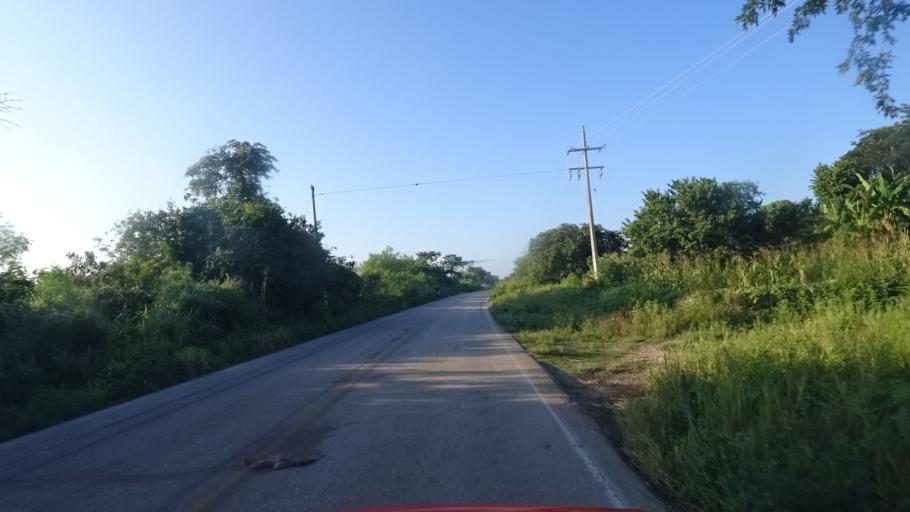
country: MX
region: Yucatan
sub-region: Panaba
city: Loche
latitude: 21.3898
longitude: -88.1420
